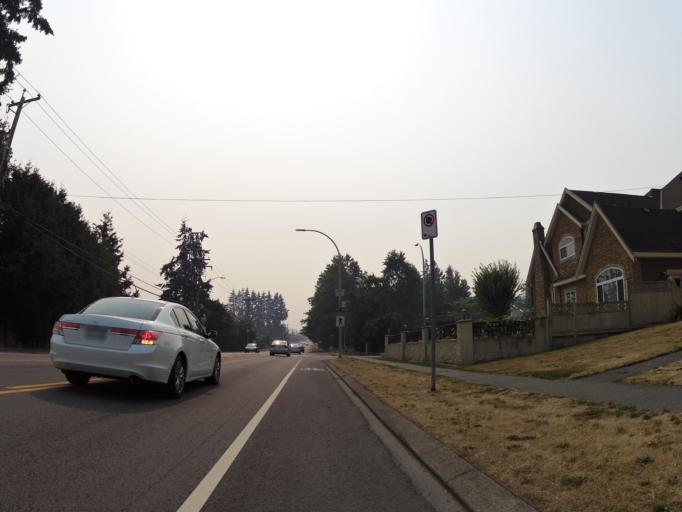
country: CA
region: British Columbia
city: Surrey
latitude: 49.1226
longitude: -122.8566
